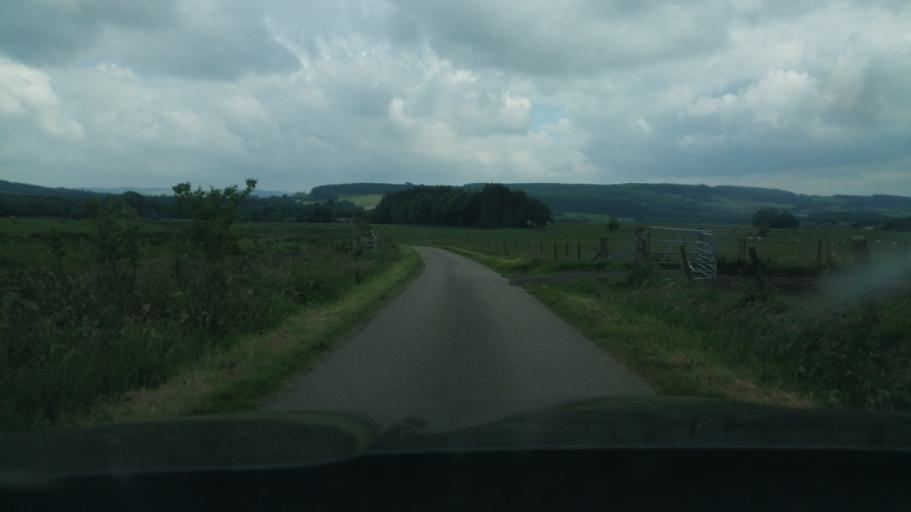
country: GB
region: Scotland
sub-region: Moray
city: Cullen
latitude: 57.5920
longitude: -2.8228
